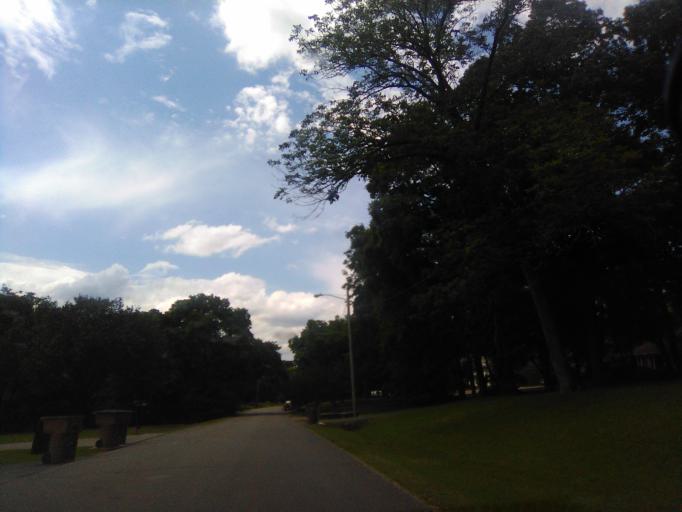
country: US
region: Tennessee
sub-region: Davidson County
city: Belle Meade
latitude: 36.1232
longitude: -86.8776
